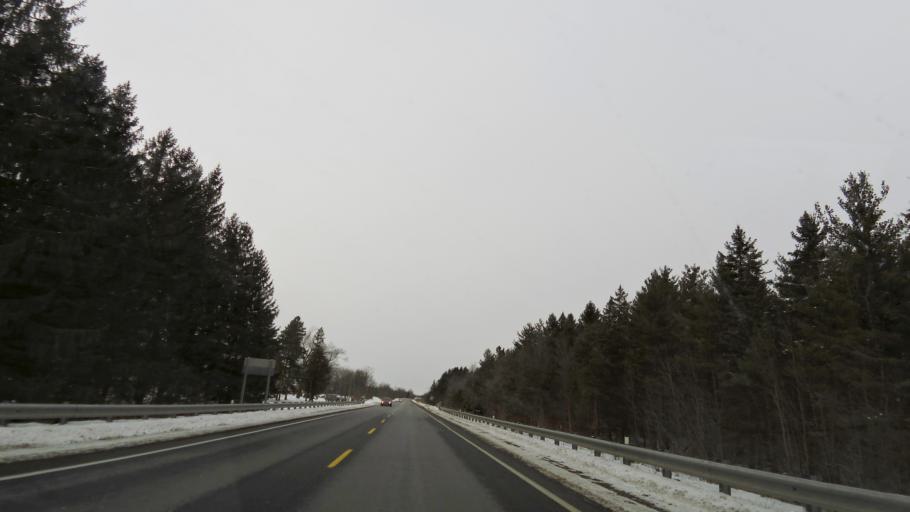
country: CA
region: Ontario
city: Cambridge
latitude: 43.3065
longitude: -80.1435
